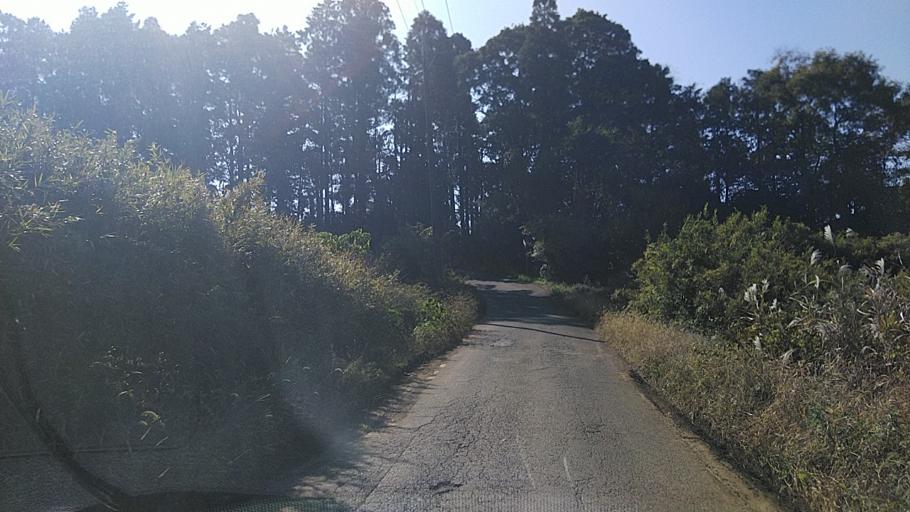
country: JP
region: Chiba
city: Sawara
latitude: 35.8448
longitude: 140.4664
